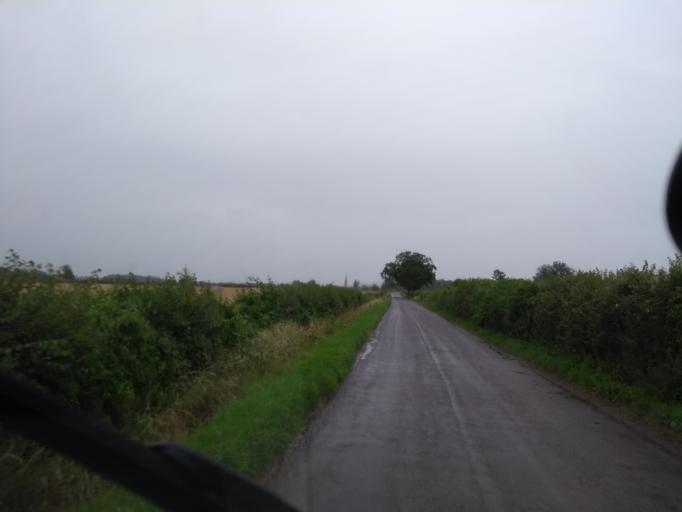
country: GB
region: England
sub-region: Somerset
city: Street
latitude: 51.0890
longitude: -2.6858
